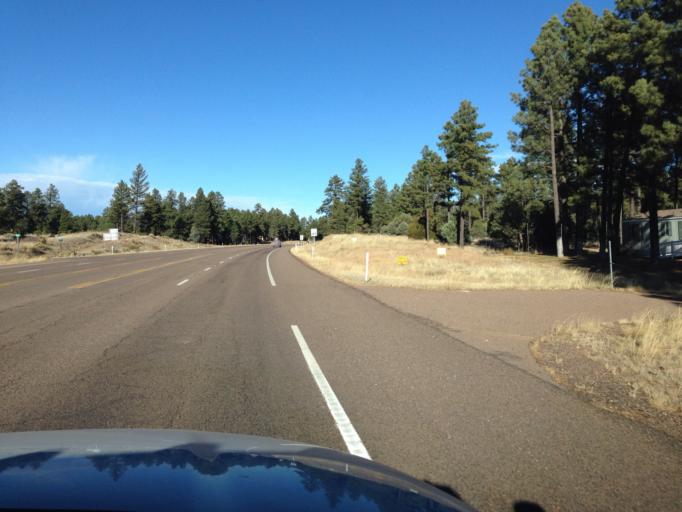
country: US
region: Arizona
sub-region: Navajo County
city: Heber-Overgaard
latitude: 34.3910
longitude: -110.5531
